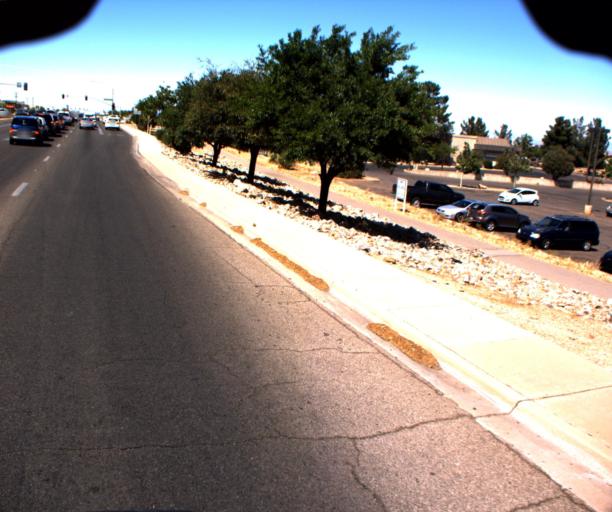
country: US
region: Arizona
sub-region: Cochise County
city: Sierra Vista
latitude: 31.5532
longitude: -110.2572
